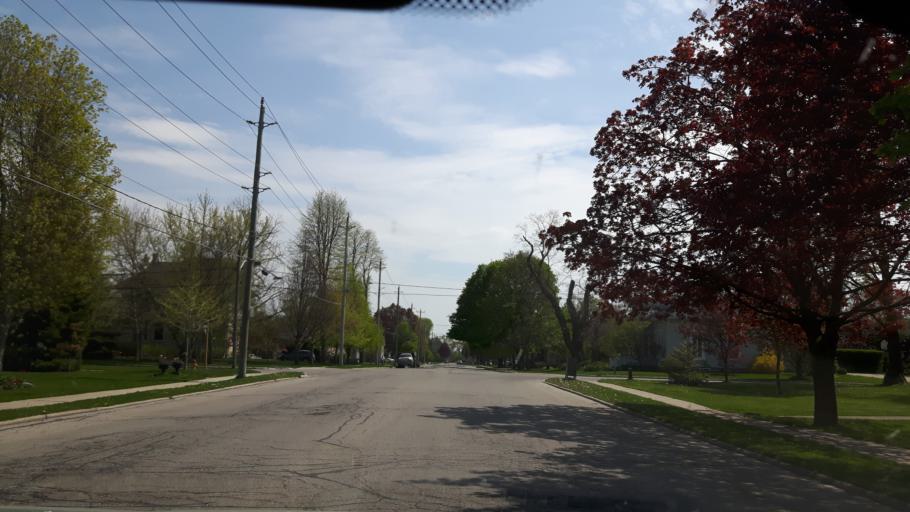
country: CA
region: Ontario
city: Goderich
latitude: 43.7426
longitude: -81.7178
